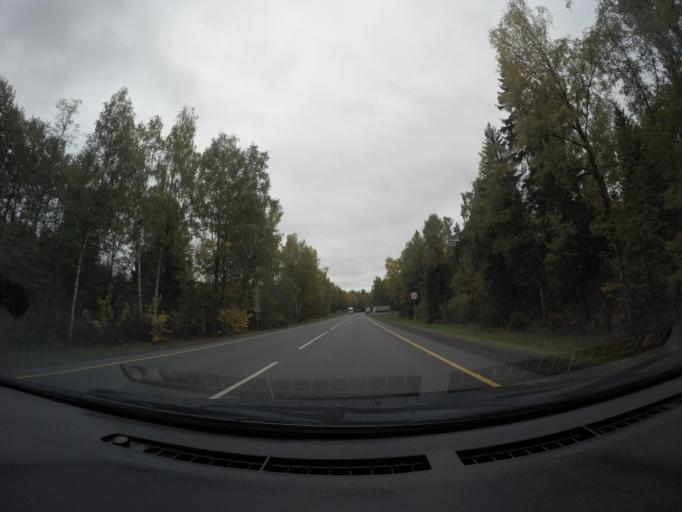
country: RU
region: Moskovskaya
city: Ruza
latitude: 55.7541
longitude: 36.2585
